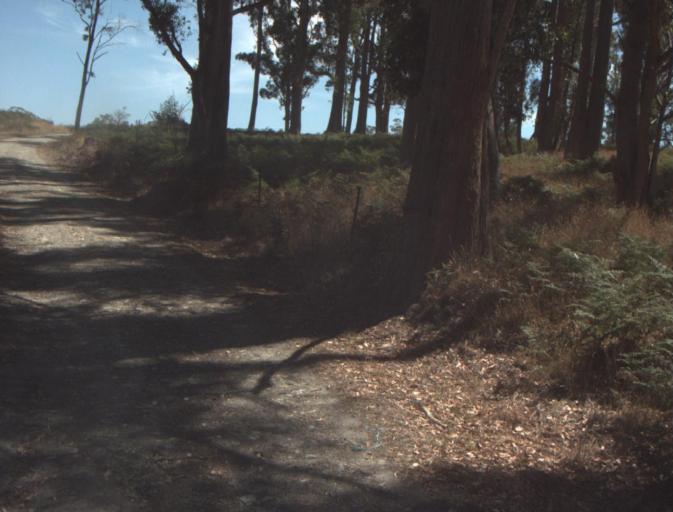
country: AU
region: Tasmania
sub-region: Launceston
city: Mayfield
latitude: -41.2489
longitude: 147.1663
